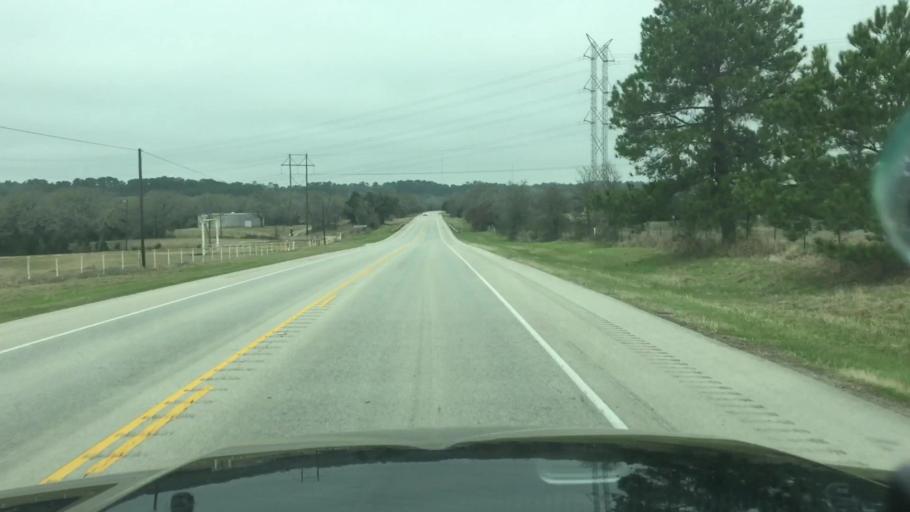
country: US
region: Texas
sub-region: Fayette County
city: La Grange
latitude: 30.0266
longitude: -96.9039
